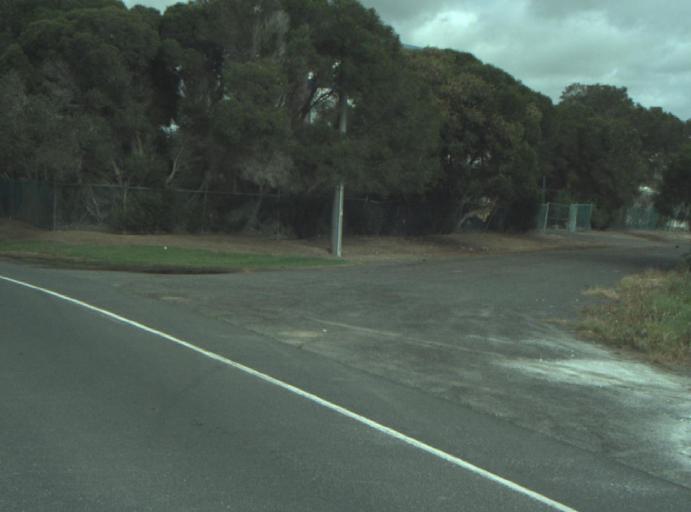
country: AU
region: Victoria
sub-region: Greater Geelong
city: Lara
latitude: -38.0777
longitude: 144.3878
